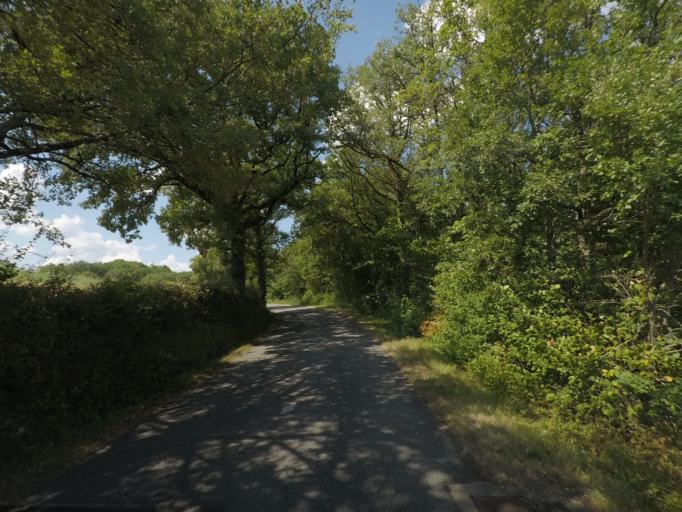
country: FR
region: Midi-Pyrenees
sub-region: Departement du Lot
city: Cahors
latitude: 44.5729
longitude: 1.5798
